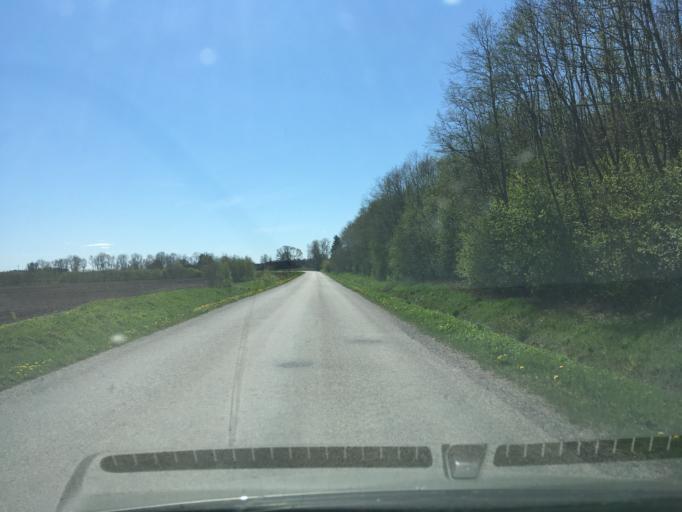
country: EE
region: Harju
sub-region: Raasiku vald
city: Arukula
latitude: 59.3961
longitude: 25.0796
